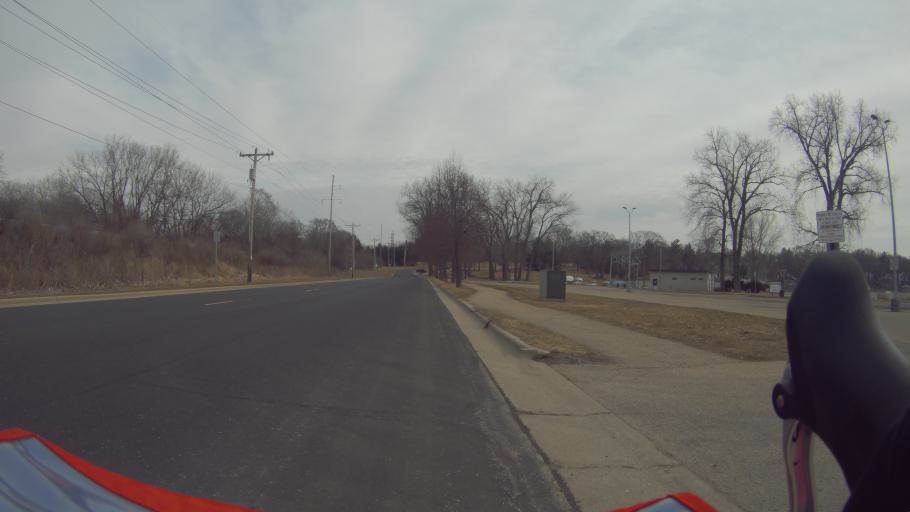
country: US
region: Wisconsin
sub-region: Dane County
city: Maple Bluff
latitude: 43.1255
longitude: -89.3760
